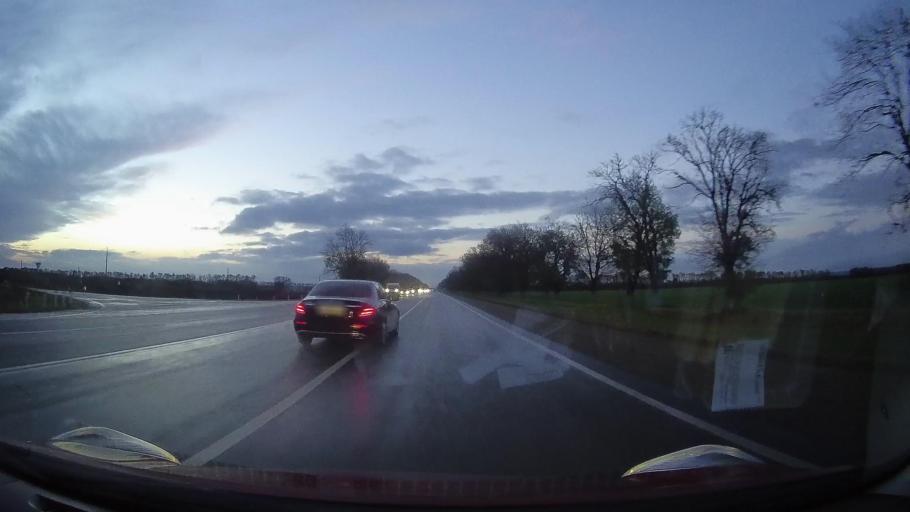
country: RU
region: Krasnodarskiy
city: Zavetnyy
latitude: 44.8870
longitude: 41.2149
